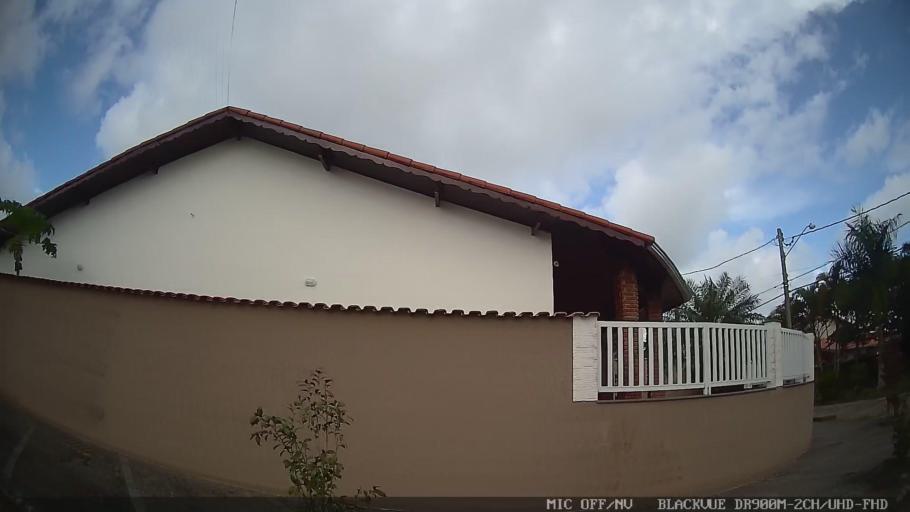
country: BR
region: Sao Paulo
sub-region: Itanhaem
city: Itanhaem
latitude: -24.2149
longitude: -46.8462
